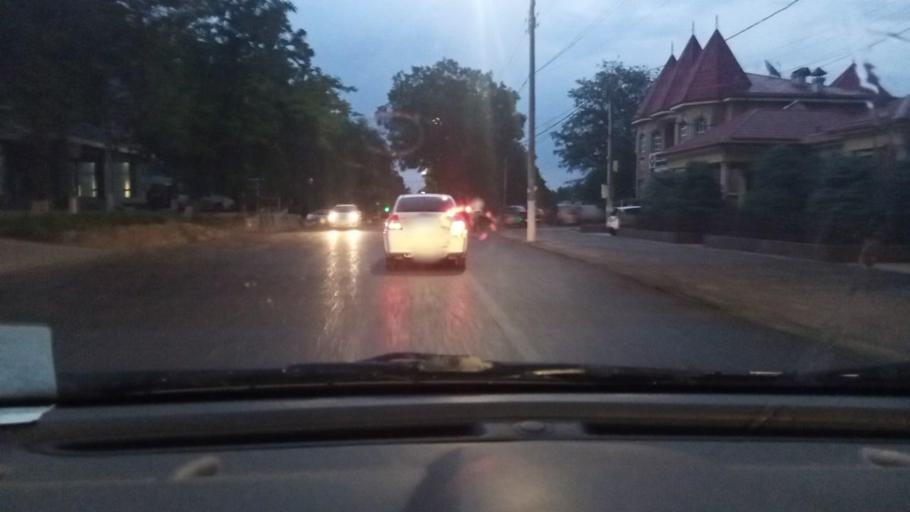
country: UZ
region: Toshkent
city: Salor
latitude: 41.3189
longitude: 69.3407
